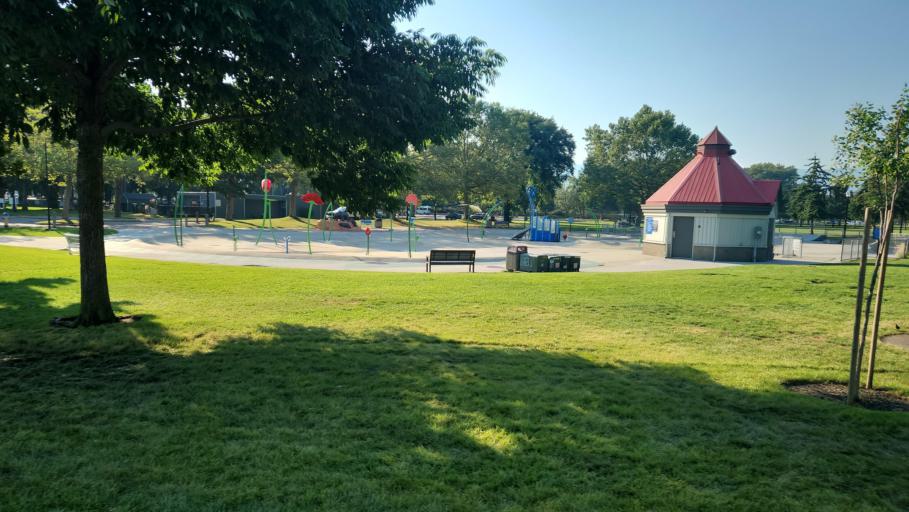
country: CA
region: British Columbia
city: Kelowna
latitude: 49.8849
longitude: -119.5033
